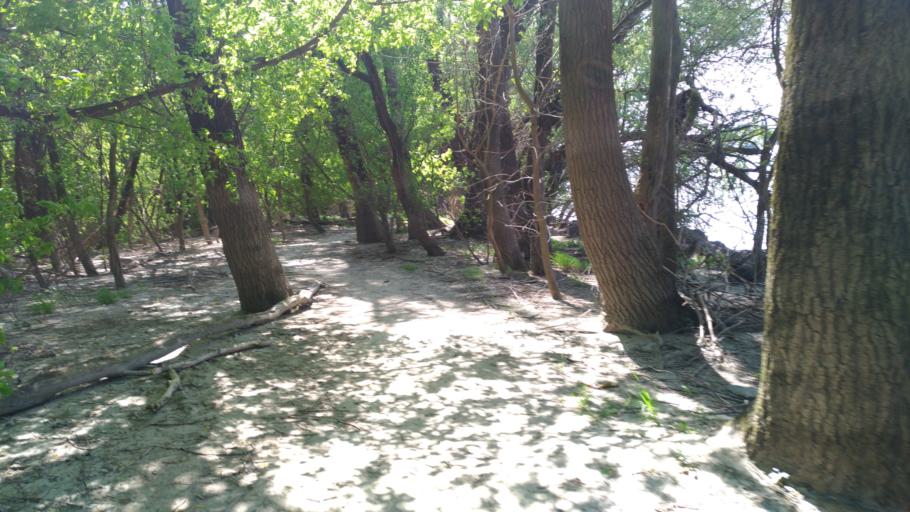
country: HU
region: Budapest
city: Budapest IV. keruelet
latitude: 47.5808
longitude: 19.0737
